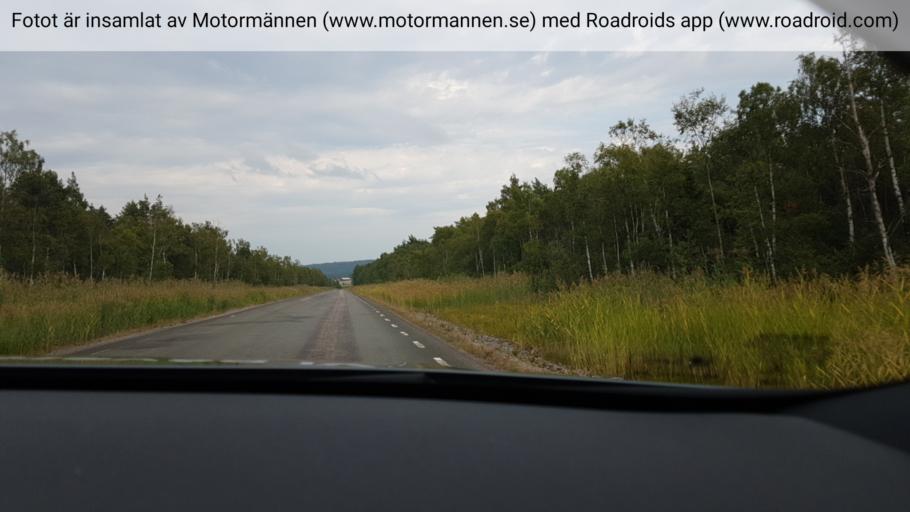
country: SE
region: Vaestra Goetaland
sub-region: Falkopings Kommun
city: Akarp
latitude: 58.1783
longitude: 13.6600
